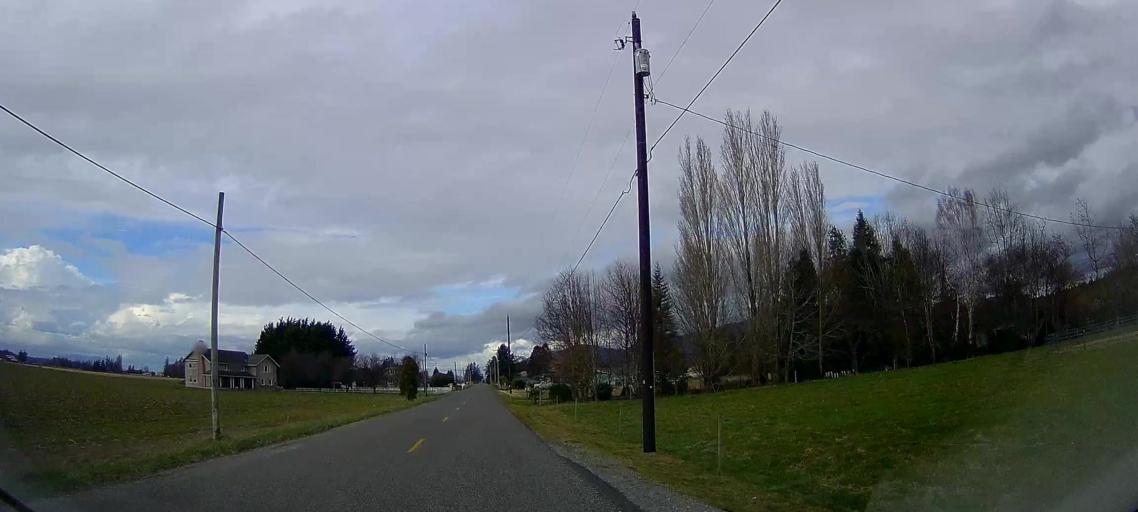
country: US
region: Washington
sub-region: Skagit County
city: Burlington
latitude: 48.5472
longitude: -122.3956
